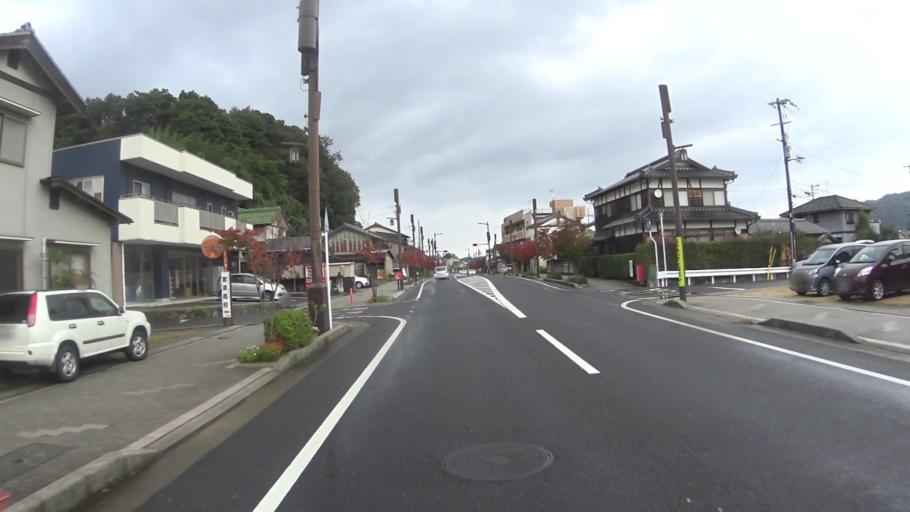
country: JP
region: Kyoto
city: Miyazu
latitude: 35.5300
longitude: 135.1915
